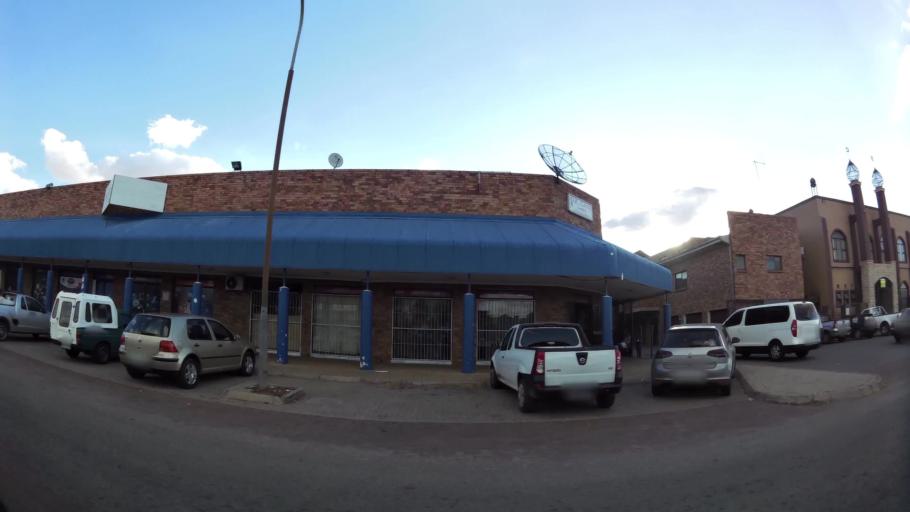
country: ZA
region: North-West
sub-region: Dr Kenneth Kaunda District Municipality
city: Potchefstroom
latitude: -26.7137
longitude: 27.0962
